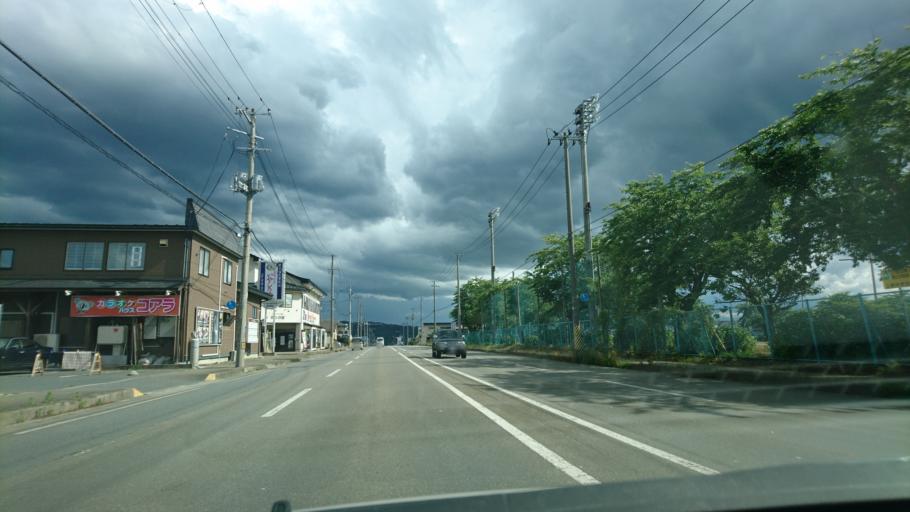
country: JP
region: Iwate
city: Kitakami
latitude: 39.3028
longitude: 141.1283
